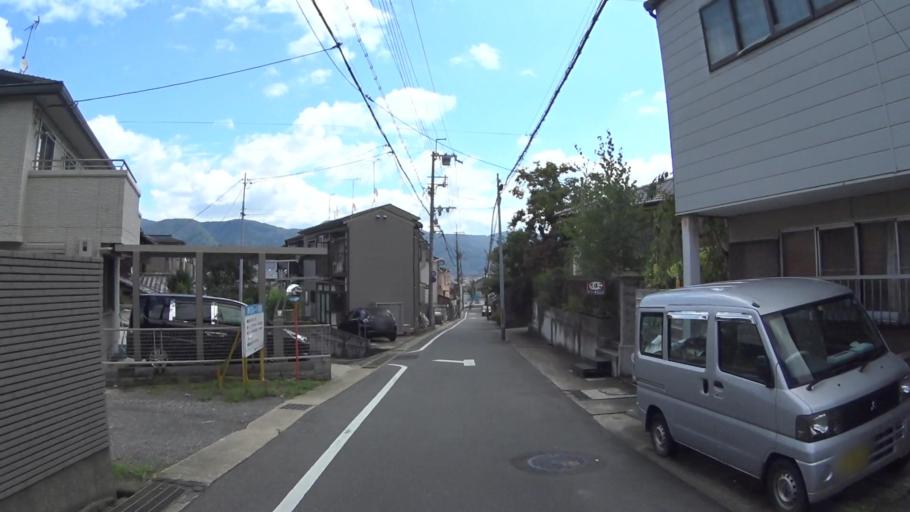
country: JP
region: Kyoto
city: Kyoto
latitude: 34.9726
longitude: 135.7951
